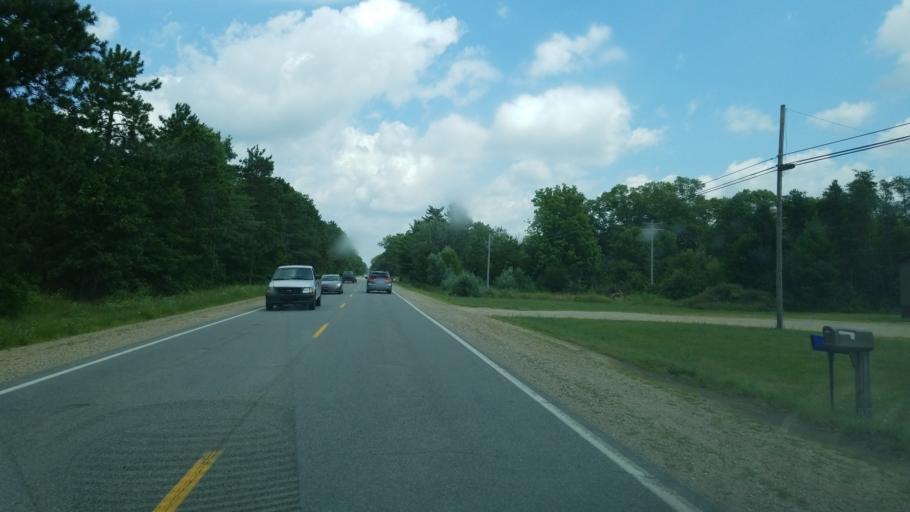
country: US
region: Michigan
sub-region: Montcalm County
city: Howard City
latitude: 43.4125
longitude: -85.4656
